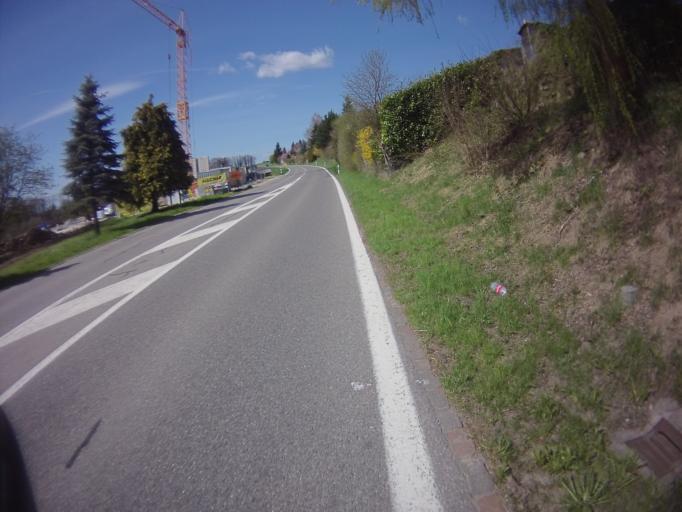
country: CH
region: Aargau
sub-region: Bezirk Bremgarten
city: Rudolfstetten
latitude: 47.3730
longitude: 8.3564
